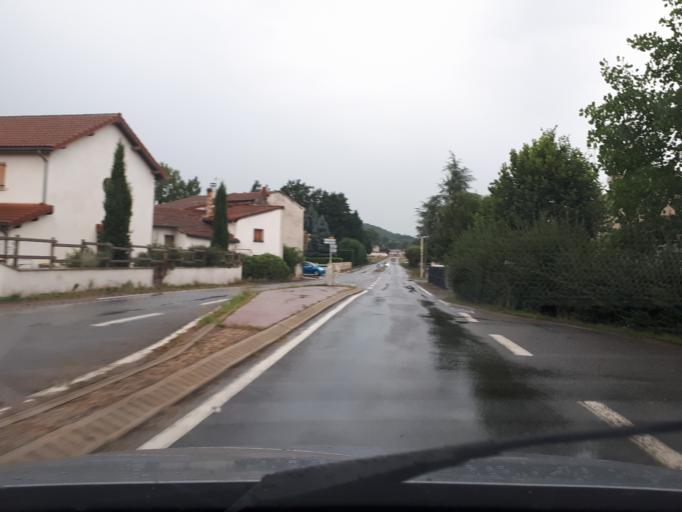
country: FR
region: Rhone-Alpes
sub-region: Departement de la Loire
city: Bellegarde-en-Forez
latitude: 45.7090
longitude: 4.2993
